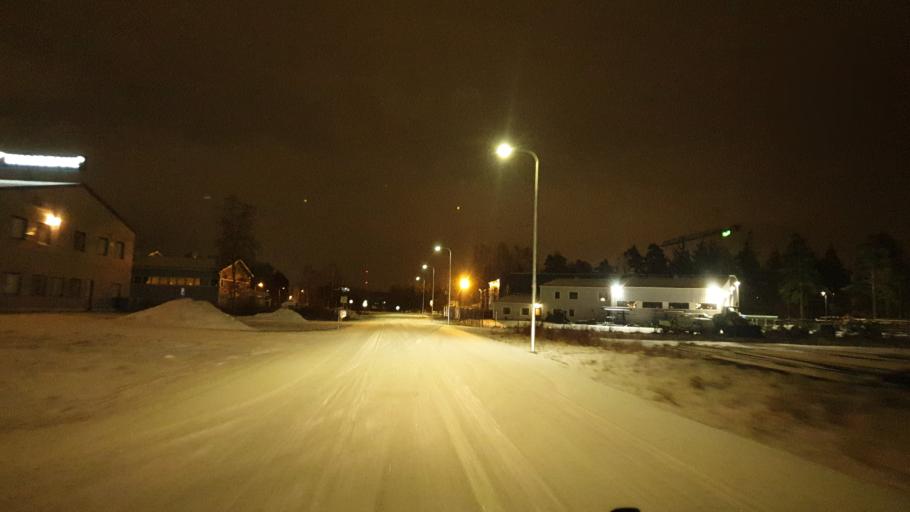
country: FI
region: Northern Ostrobothnia
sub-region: Oulu
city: Oulu
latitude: 64.9944
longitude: 25.4453
